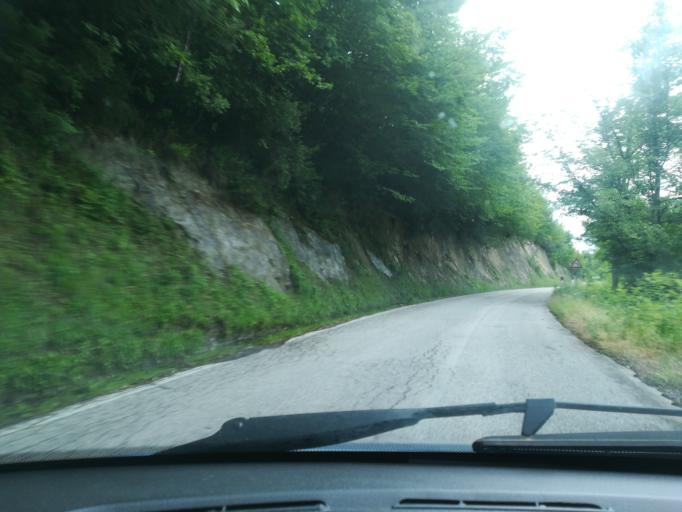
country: IT
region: The Marches
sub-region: Province of Fermo
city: Montefortino
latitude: 42.9380
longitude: 13.3610
